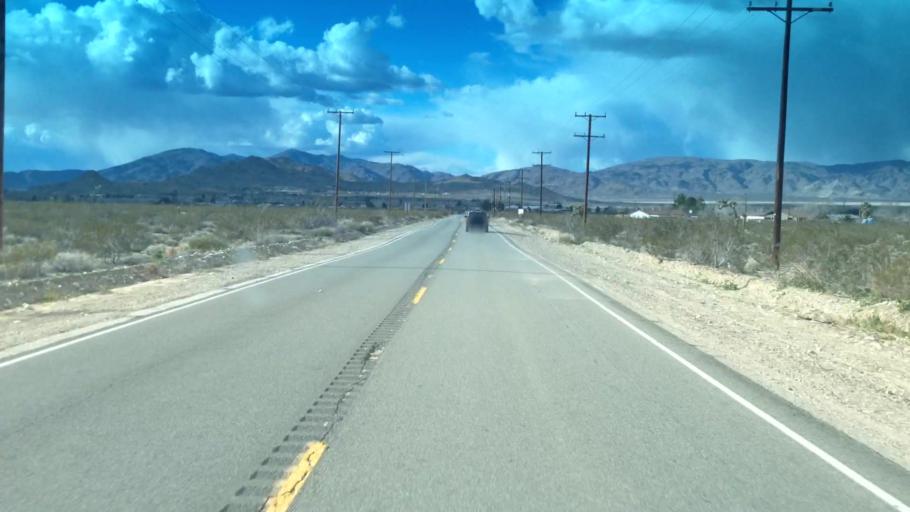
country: US
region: California
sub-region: San Bernardino County
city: Lucerne Valley
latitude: 34.4319
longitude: -116.9344
